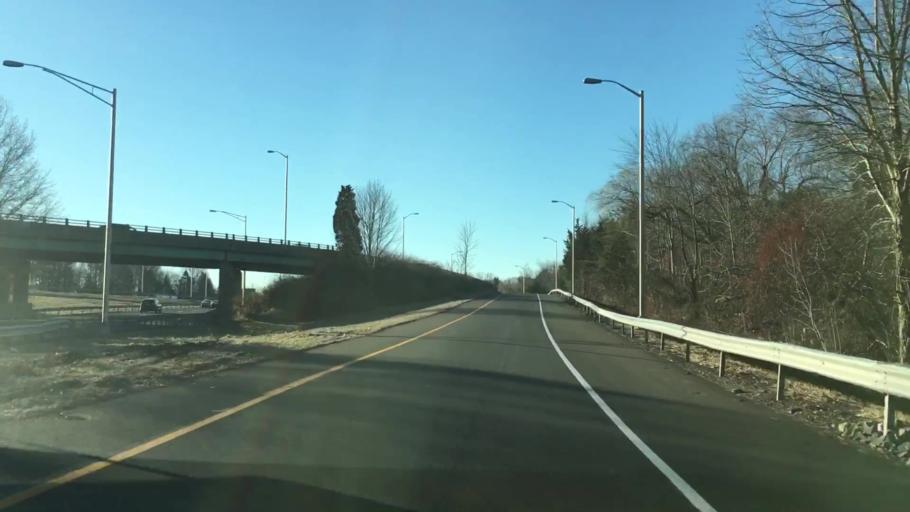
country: US
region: Connecticut
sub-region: New Haven County
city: Meriden
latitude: 41.5332
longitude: -72.7695
